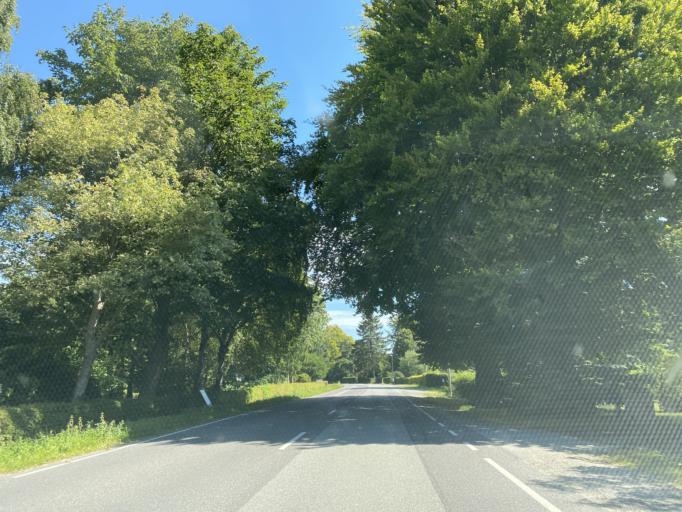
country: DK
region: South Denmark
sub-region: Faaborg-Midtfyn Kommune
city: Ringe
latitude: 55.2068
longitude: 10.3477
